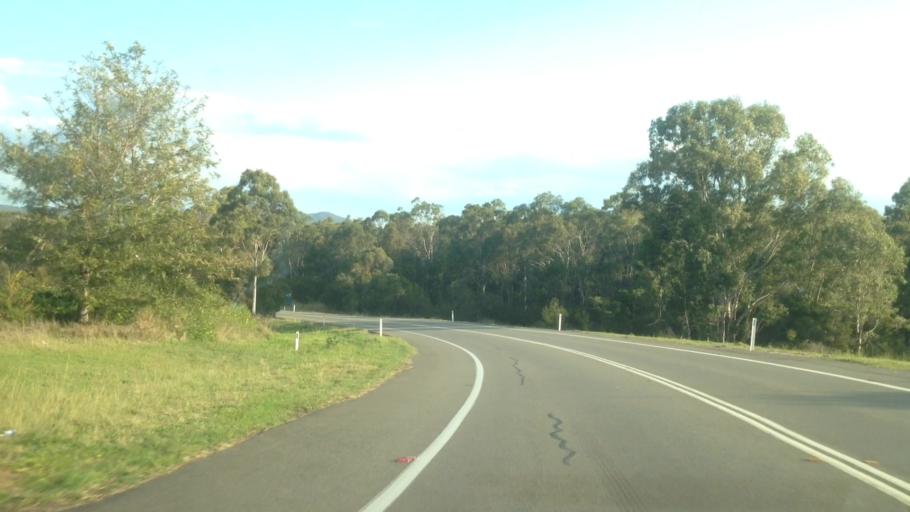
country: AU
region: New South Wales
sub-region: Cessnock
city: Kurri Kurri
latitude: -32.8338
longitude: 151.4804
